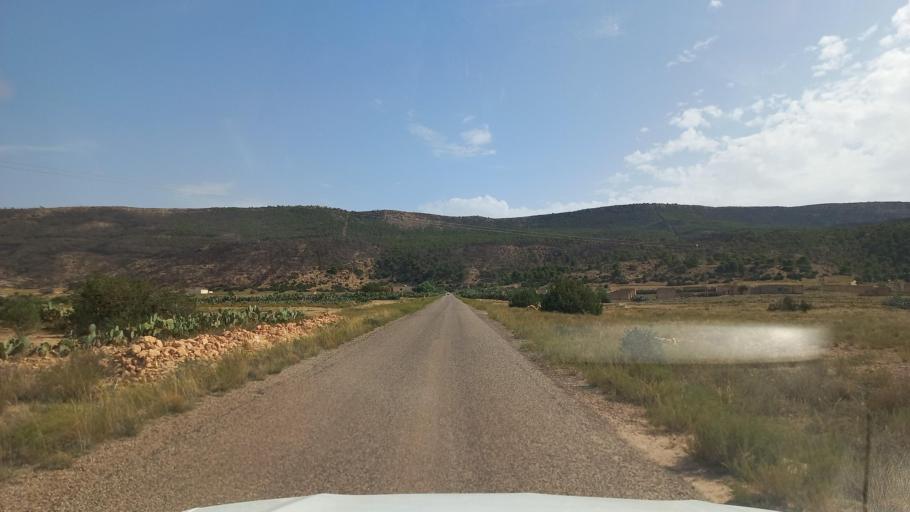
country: TN
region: Al Qasrayn
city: Kasserine
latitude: 35.3577
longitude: 8.8861
